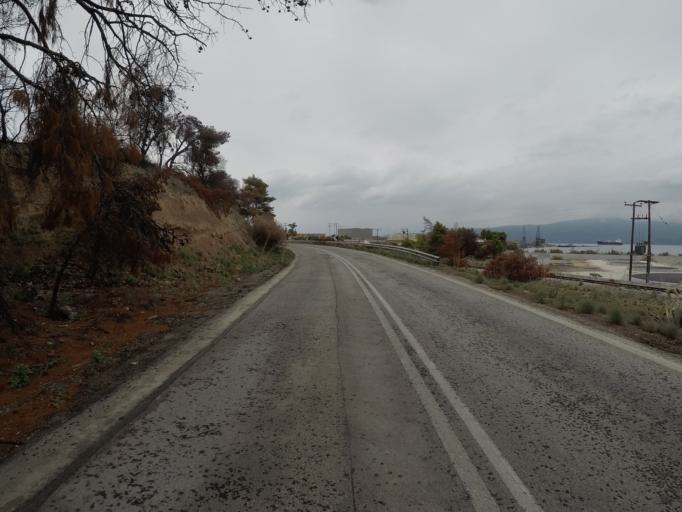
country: GR
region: Peloponnese
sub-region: Nomos Korinthias
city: Isthmia
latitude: 37.9214
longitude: 23.0550
